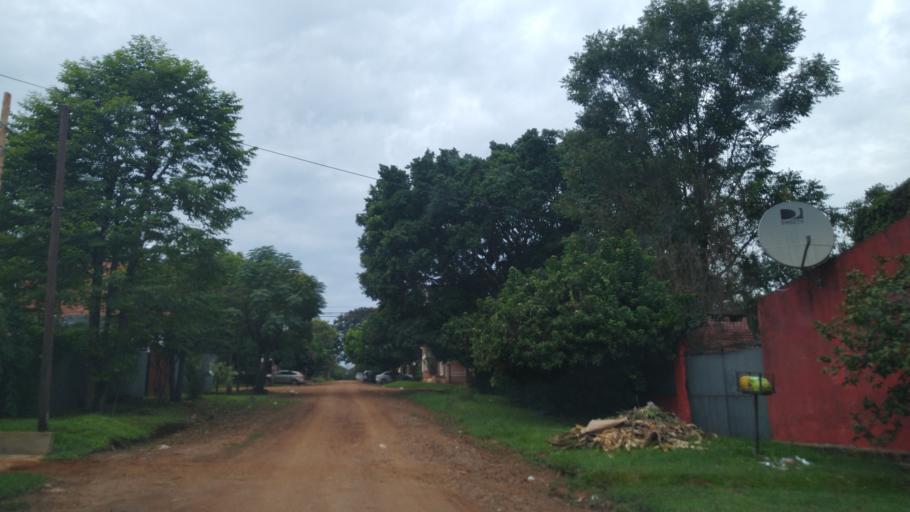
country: AR
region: Misiones
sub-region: Departamento de Capital
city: Posadas
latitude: -27.3683
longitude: -55.9308
